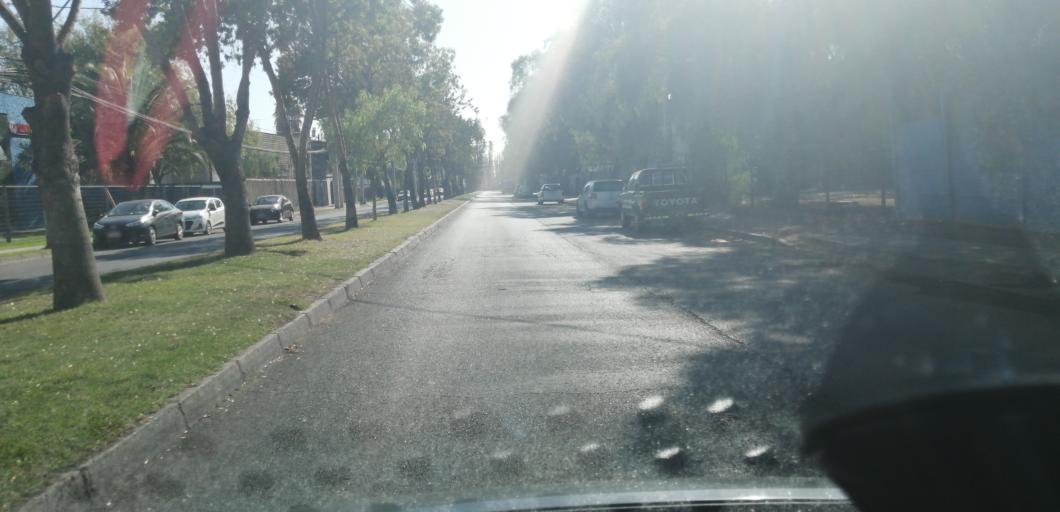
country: CL
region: Santiago Metropolitan
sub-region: Provincia de Santiago
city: Lo Prado
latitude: -33.3818
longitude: -70.7739
